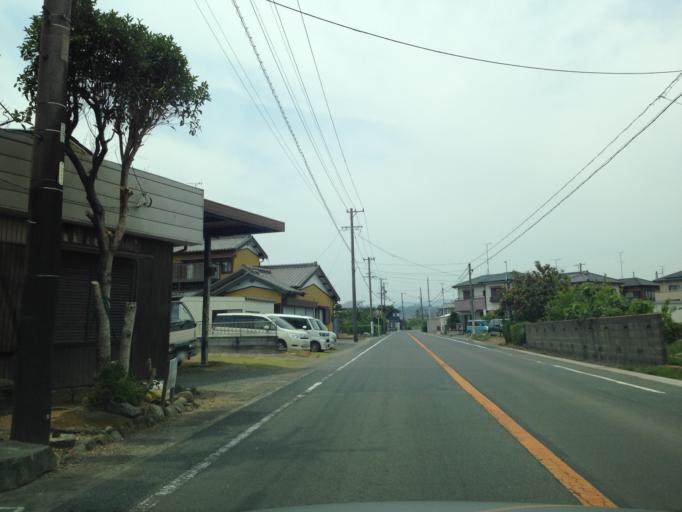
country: JP
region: Shizuoka
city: Hamakita
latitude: 34.8163
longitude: 137.7766
